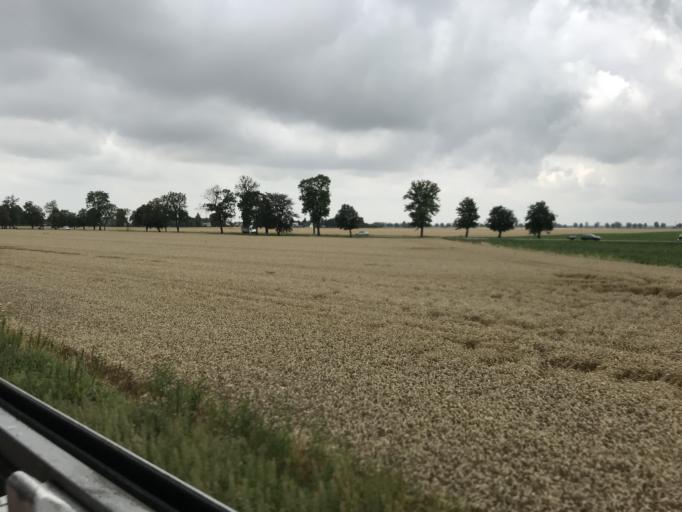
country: PL
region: Pomeranian Voivodeship
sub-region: Powiat malborski
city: Stare Pole
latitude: 54.0465
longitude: 19.1706
